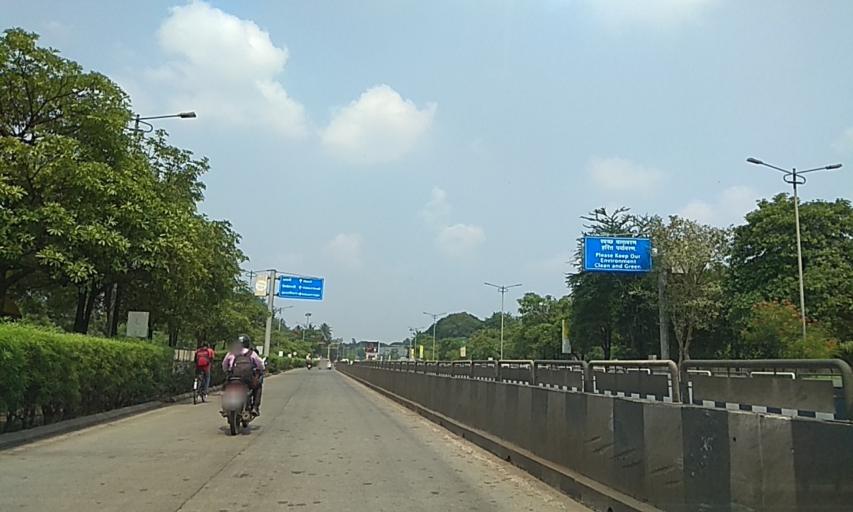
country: IN
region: Maharashtra
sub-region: Pune Division
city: Khadki
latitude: 18.5508
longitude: 73.8723
